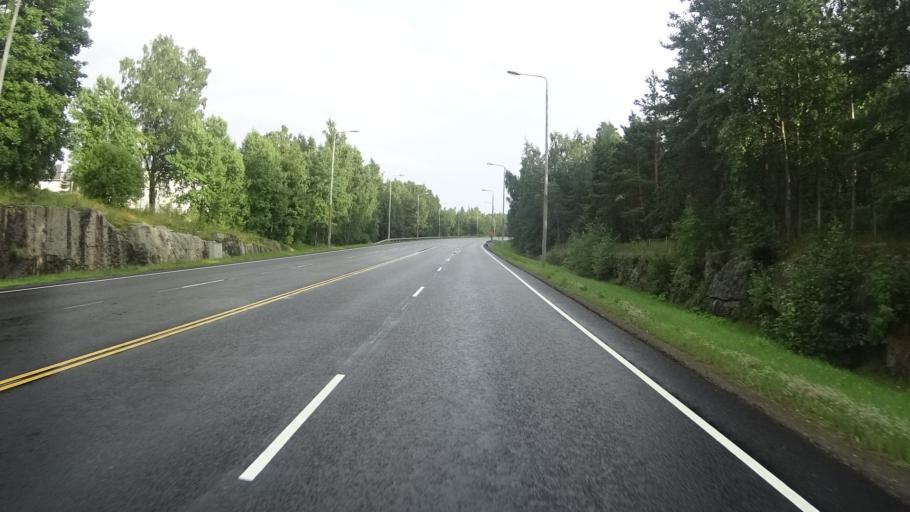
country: FI
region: Kymenlaakso
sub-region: Kotka-Hamina
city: Kotka
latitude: 60.4787
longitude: 26.9151
